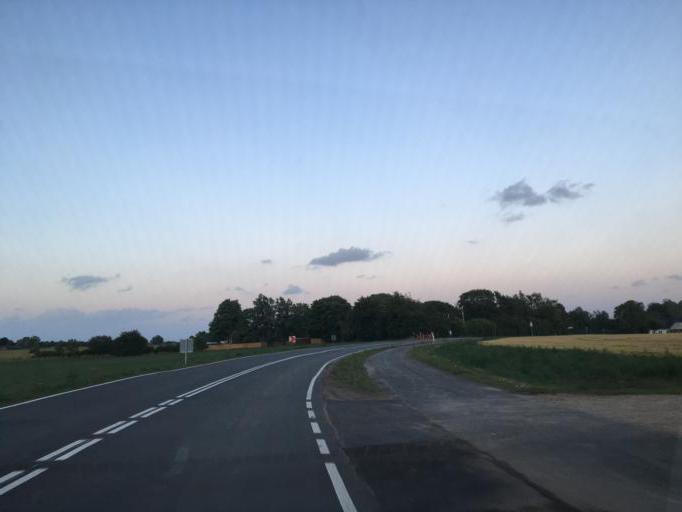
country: DK
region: Zealand
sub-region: Solrod Kommune
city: Havdrup
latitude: 55.5185
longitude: 12.1414
